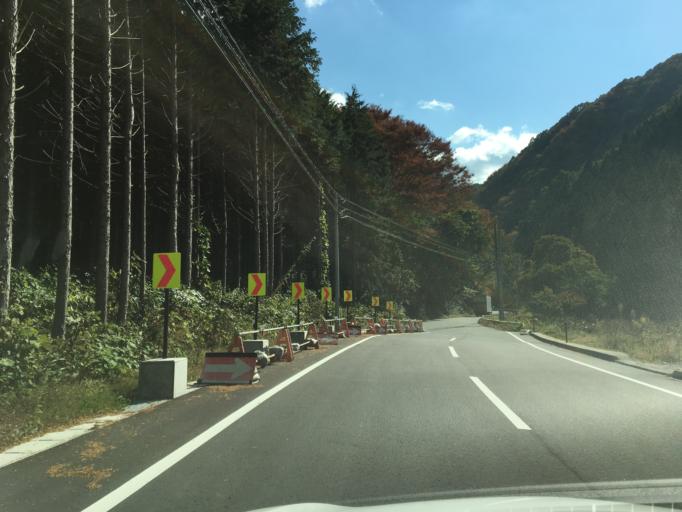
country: JP
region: Fukushima
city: Namie
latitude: 37.3493
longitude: 140.8842
